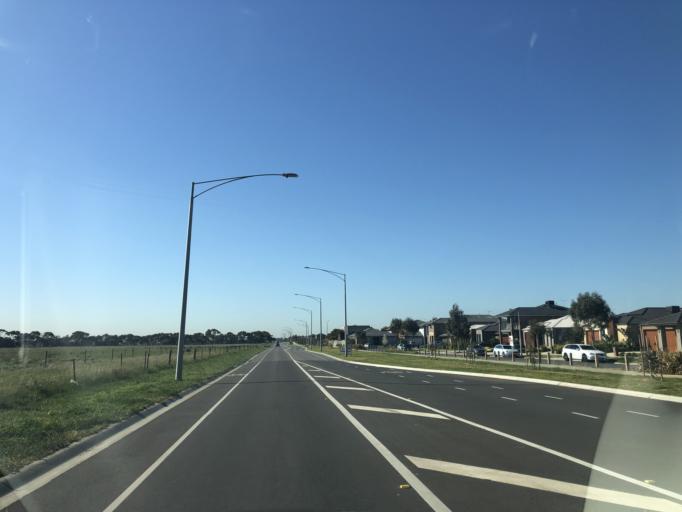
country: AU
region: Victoria
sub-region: Wyndham
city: Hoppers Crossing
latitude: -37.9086
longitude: 144.7147
